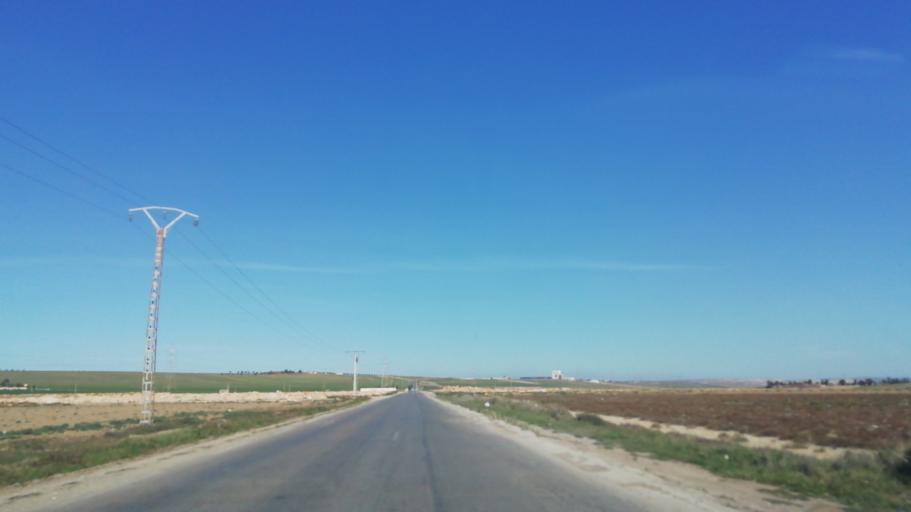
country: DZ
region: Oran
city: Es Senia
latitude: 35.5246
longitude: -0.5873
